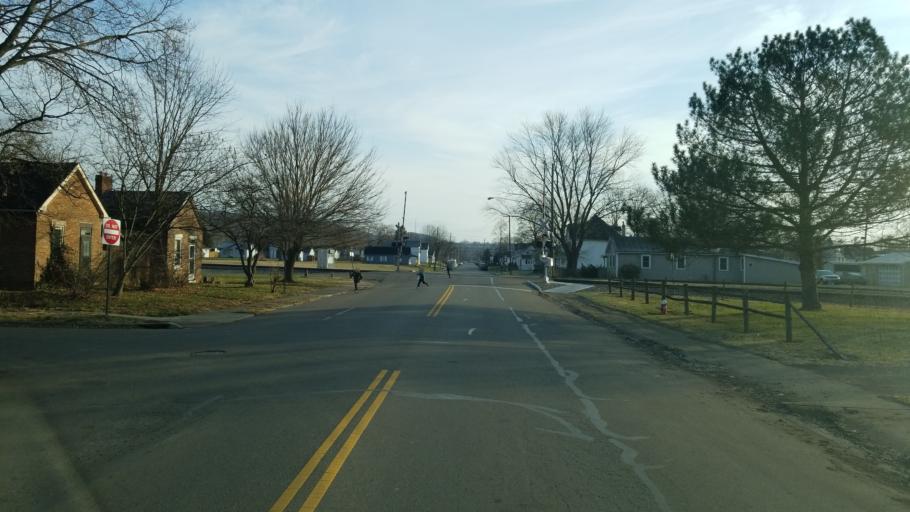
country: US
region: Ohio
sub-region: Ross County
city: Chillicothe
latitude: 39.3379
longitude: -82.9694
